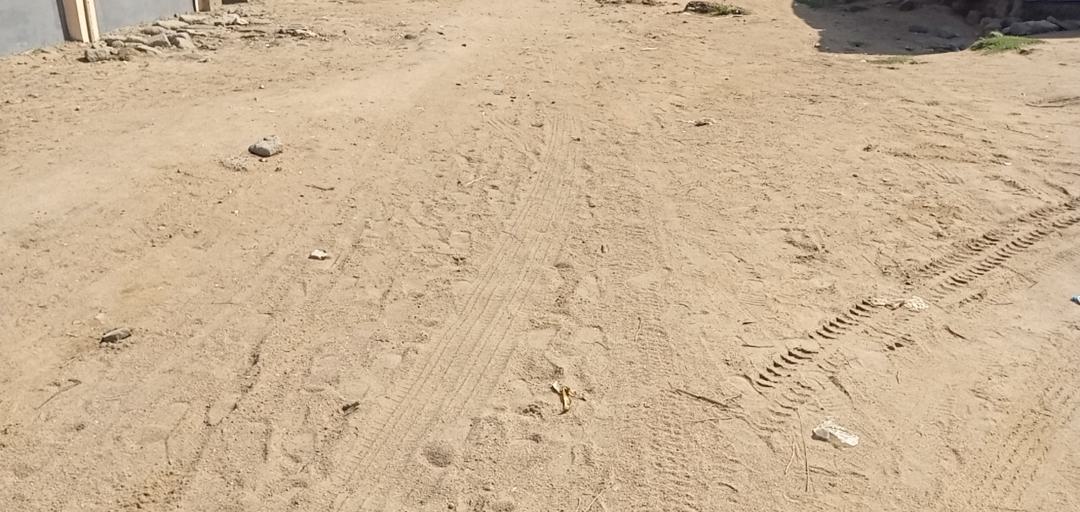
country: GH
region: Central
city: Winneba
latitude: 5.3535
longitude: -0.6229
